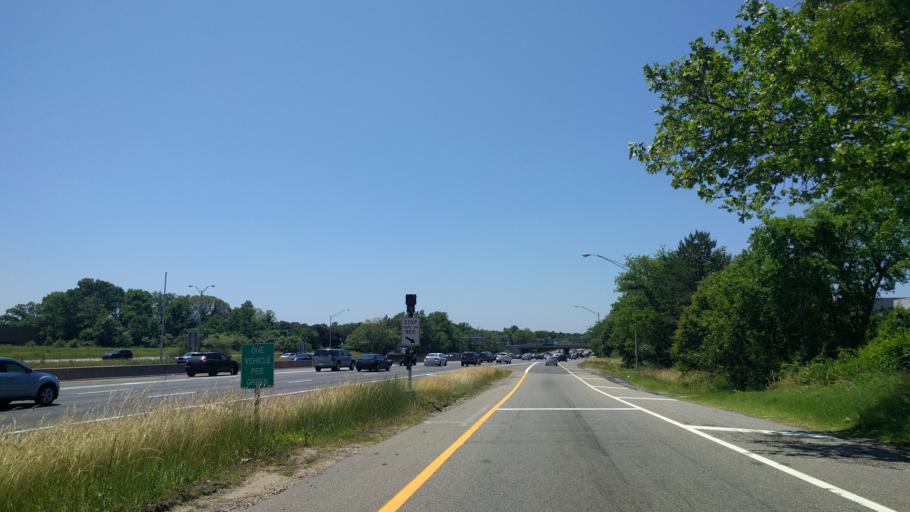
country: US
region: New York
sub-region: Suffolk County
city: Hauppauge
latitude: 40.8079
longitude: -73.2283
